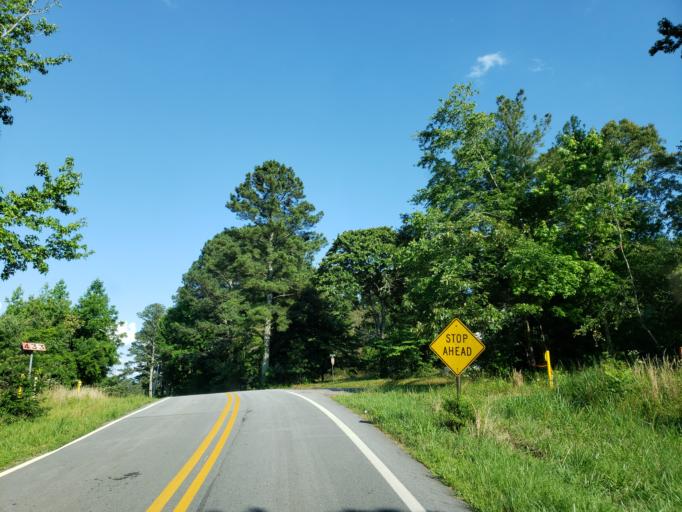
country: US
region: Georgia
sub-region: Haralson County
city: Bremen
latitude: 33.7083
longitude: -85.1169
